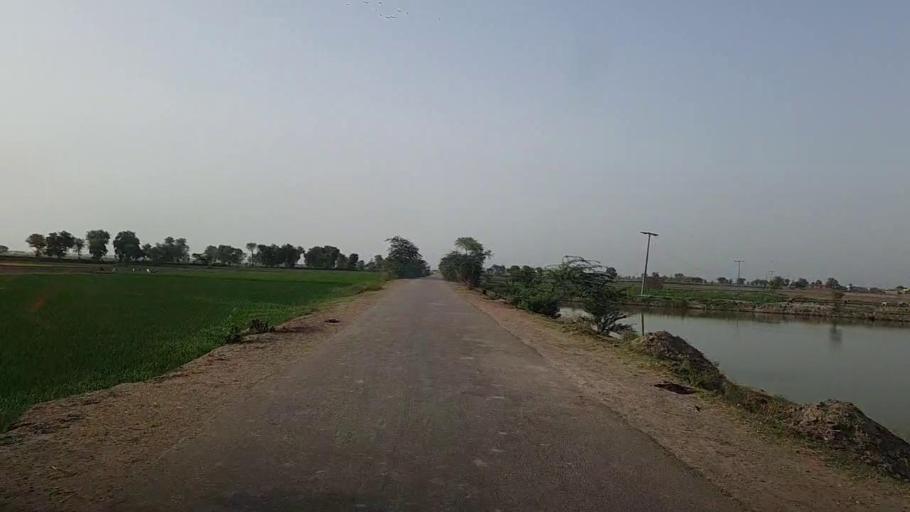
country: PK
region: Sindh
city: Khairpur Nathan Shah
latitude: 27.1071
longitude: 67.7926
